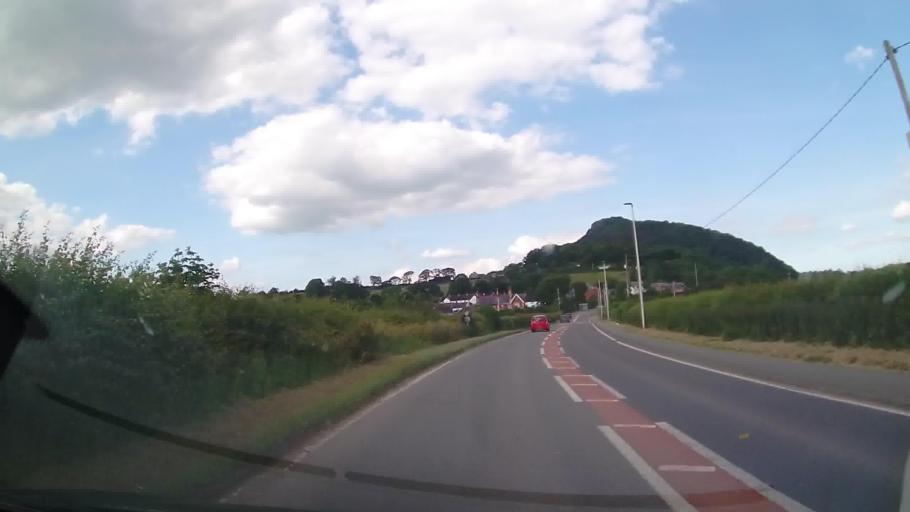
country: GB
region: Wales
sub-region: Sir Powys
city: Welshpool
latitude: 52.6936
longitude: -3.0719
